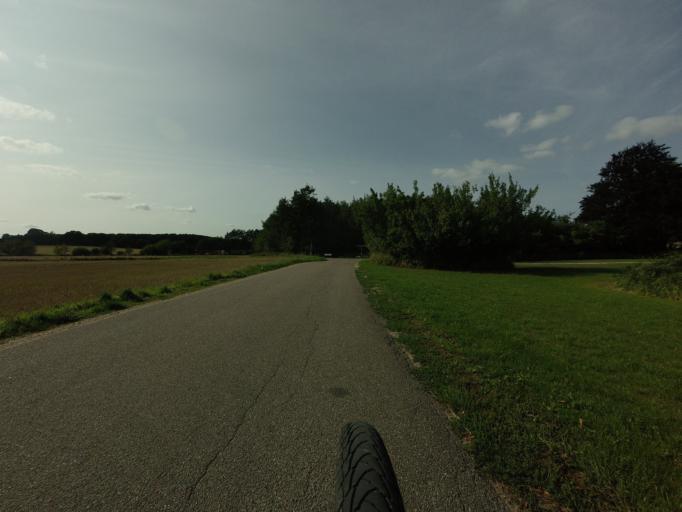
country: DK
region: Zealand
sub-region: Faxe Kommune
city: Fakse
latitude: 55.2127
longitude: 12.1293
